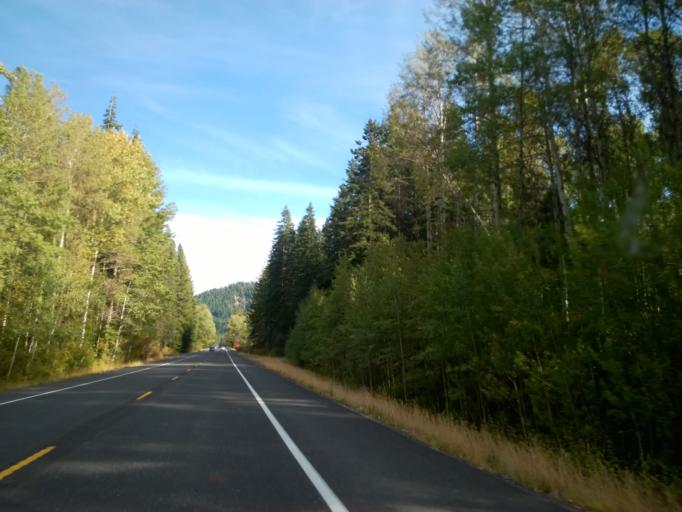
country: US
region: Washington
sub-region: Chelan County
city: Leavenworth
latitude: 47.7704
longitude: -120.8071
